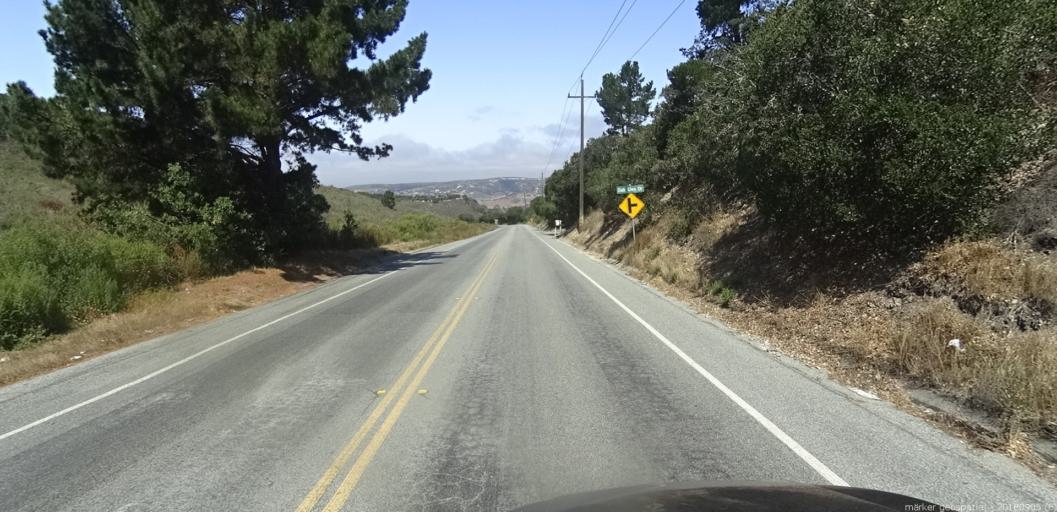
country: US
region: California
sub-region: Monterey County
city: Carmel Valley Village
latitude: 36.5498
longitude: -121.7533
